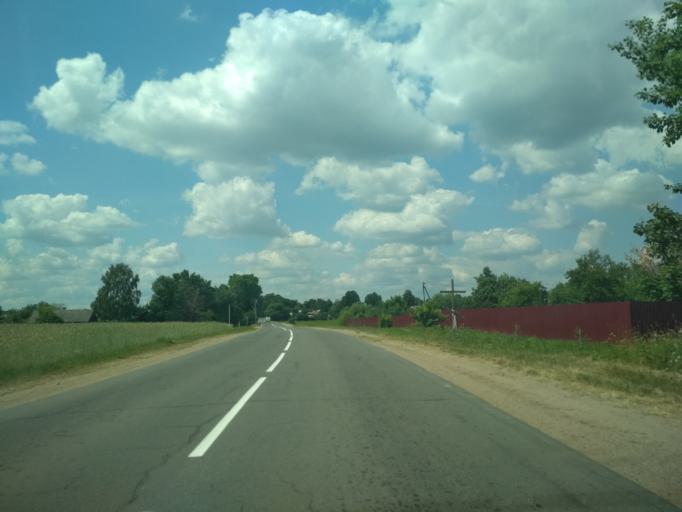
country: BY
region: Minsk
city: Svislach
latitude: 53.5703
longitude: 27.9903
